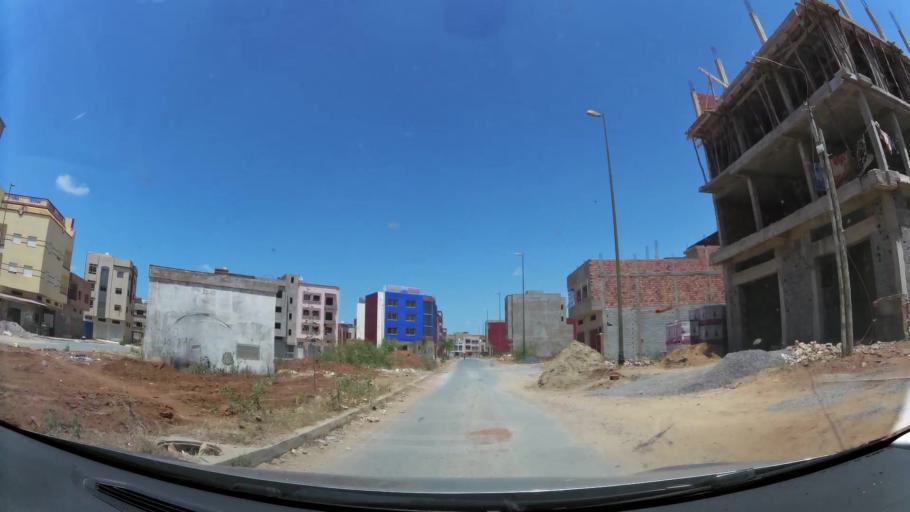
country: MA
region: Gharb-Chrarda-Beni Hssen
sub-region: Kenitra Province
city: Kenitra
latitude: 34.2319
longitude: -6.6061
